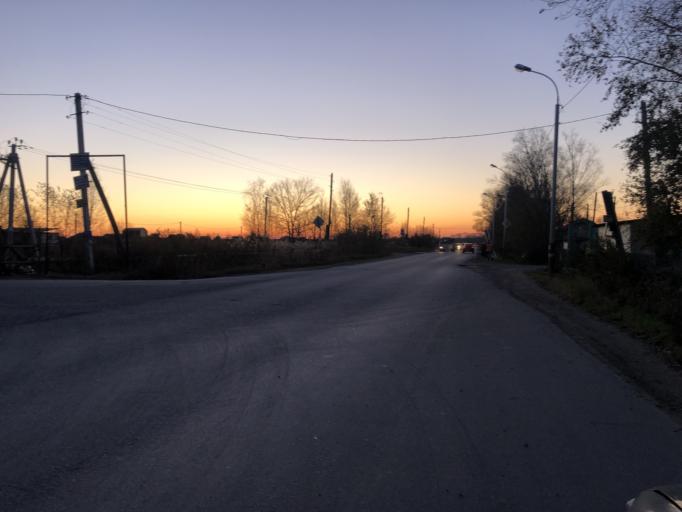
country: RU
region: Khabarovsk Krai
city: Topolevo
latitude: 48.4551
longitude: 135.1983
